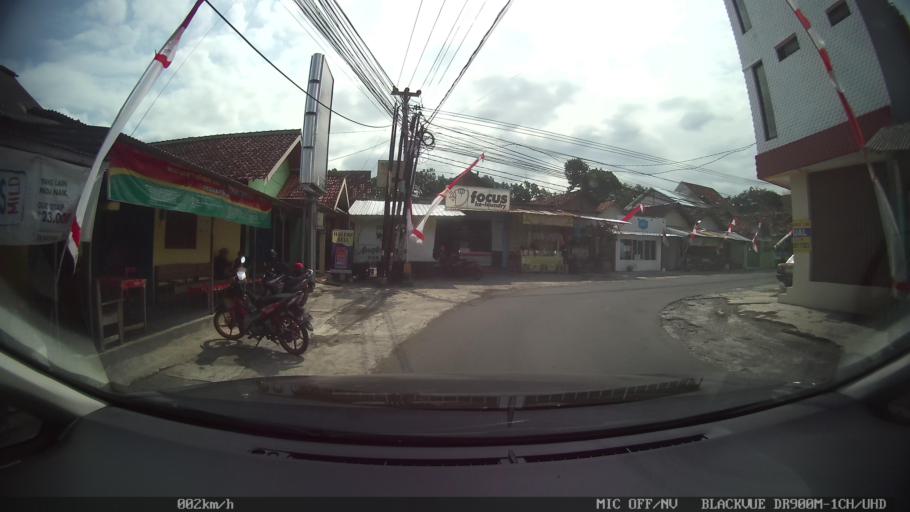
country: ID
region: Daerah Istimewa Yogyakarta
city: Depok
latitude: -7.7561
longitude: 110.4229
